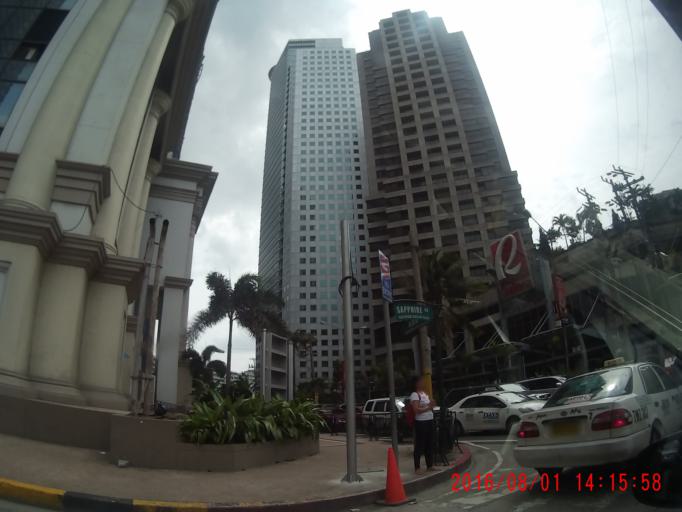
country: PH
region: Metro Manila
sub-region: Pasig
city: Pasig City
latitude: 14.5897
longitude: 121.0615
